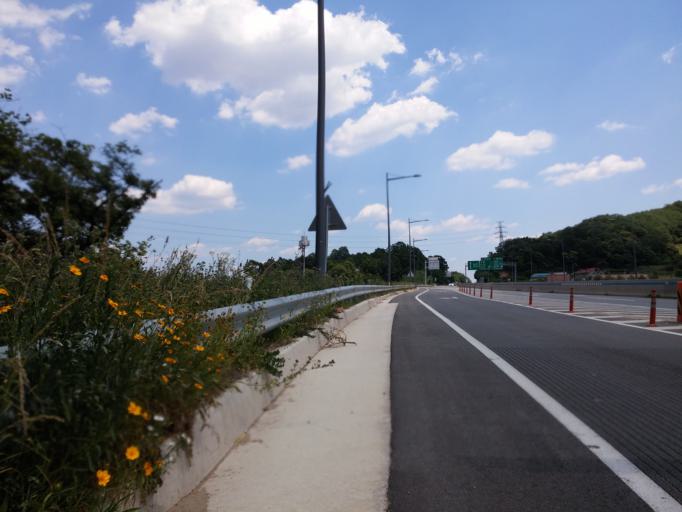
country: KR
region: Chungcheongbuk-do
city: Cheongju-si
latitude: 36.6017
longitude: 127.4436
